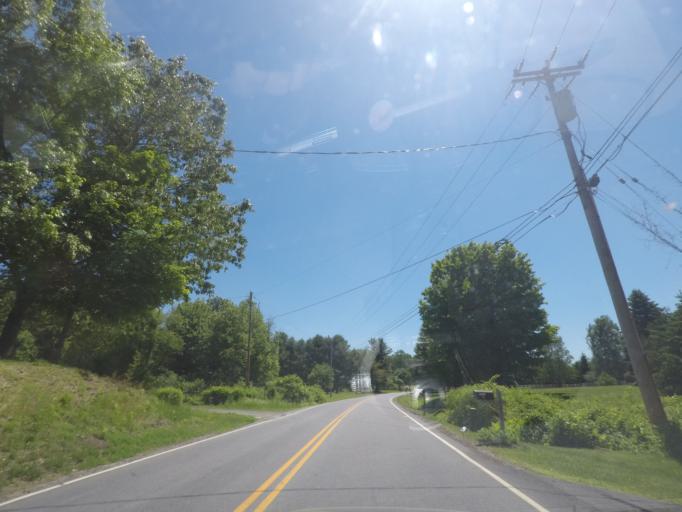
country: US
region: New York
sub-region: Saratoga County
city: Country Knolls
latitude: 42.9452
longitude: -73.7667
